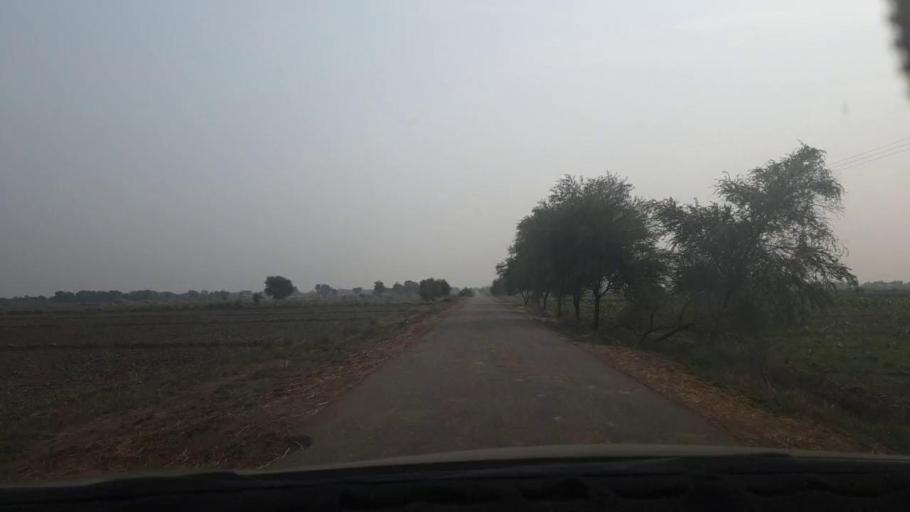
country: PK
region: Sindh
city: Jamshoro
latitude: 25.5193
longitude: 68.3145
